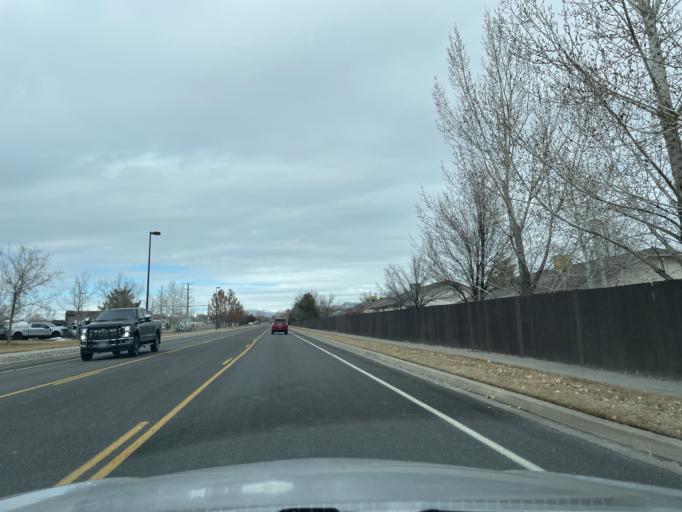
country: US
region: Colorado
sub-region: Mesa County
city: Grand Junction
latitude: 39.0959
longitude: -108.5801
